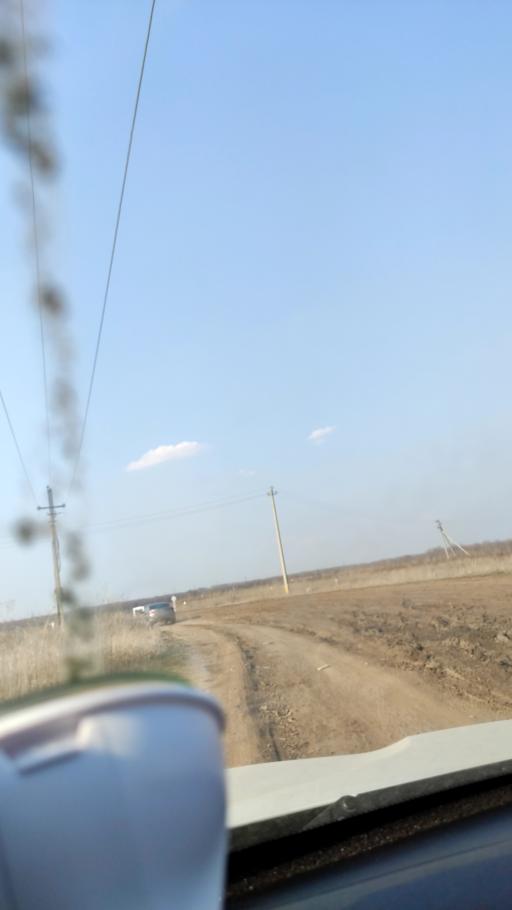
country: RU
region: Samara
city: Kinel'
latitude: 53.2557
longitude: 50.5292
